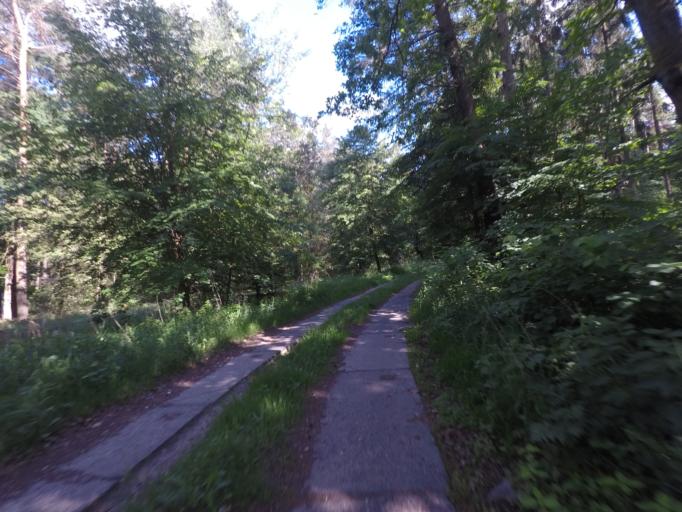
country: DE
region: Brandenburg
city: Britz
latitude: 52.8660
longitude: 13.7834
